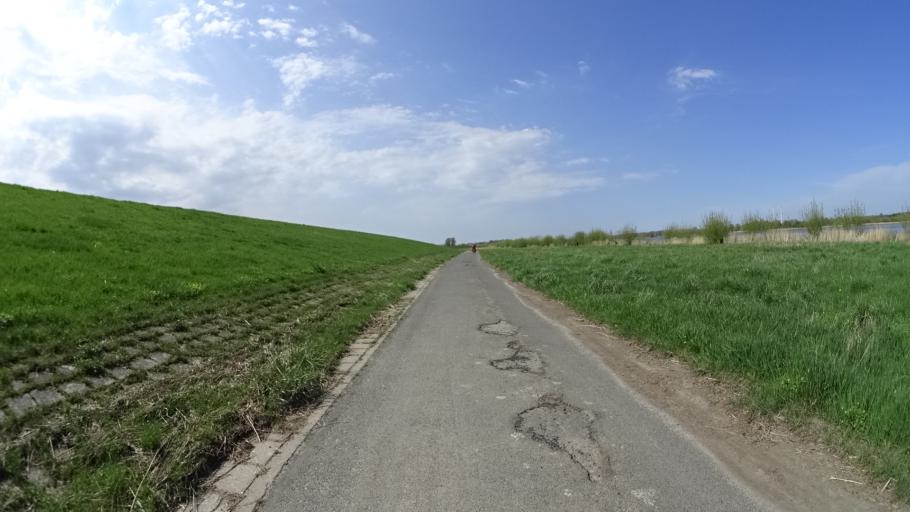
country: DE
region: Schleswig-Holstein
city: Wedel
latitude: 53.5465
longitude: 9.7556
